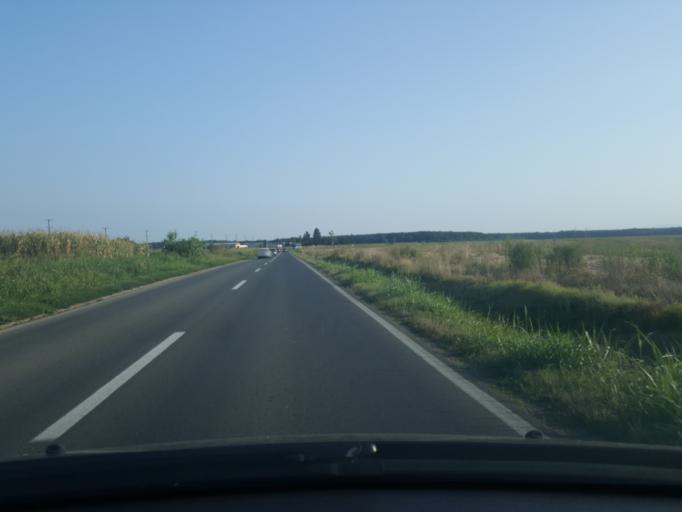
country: RS
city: Hrtkovci
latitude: 44.8549
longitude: 19.7711
